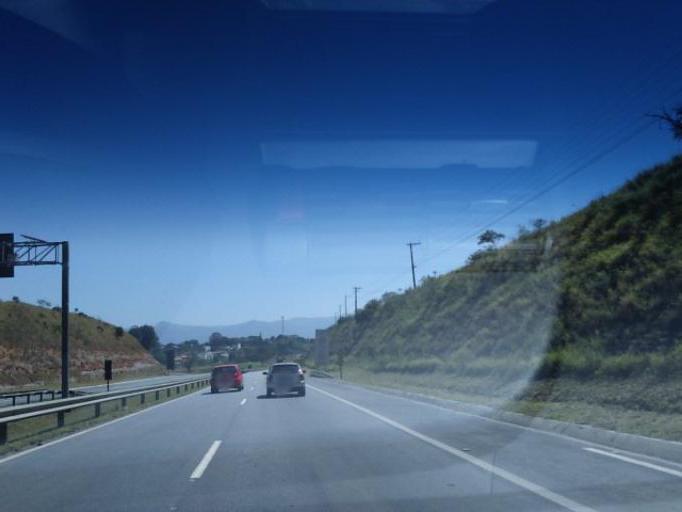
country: BR
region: Sao Paulo
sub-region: Taubate
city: Taubate
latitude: -23.0506
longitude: -45.6249
